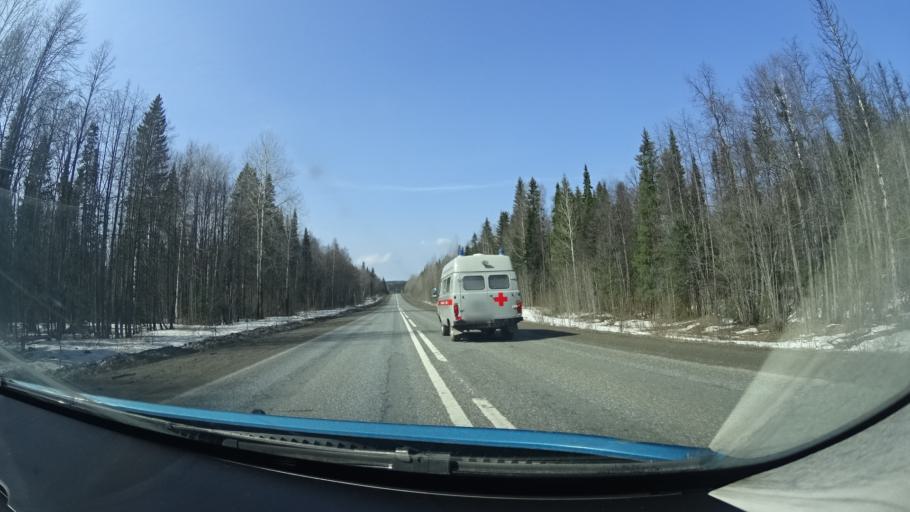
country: RU
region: Perm
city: Yugo-Kamskiy
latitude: 57.6087
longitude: 55.6466
